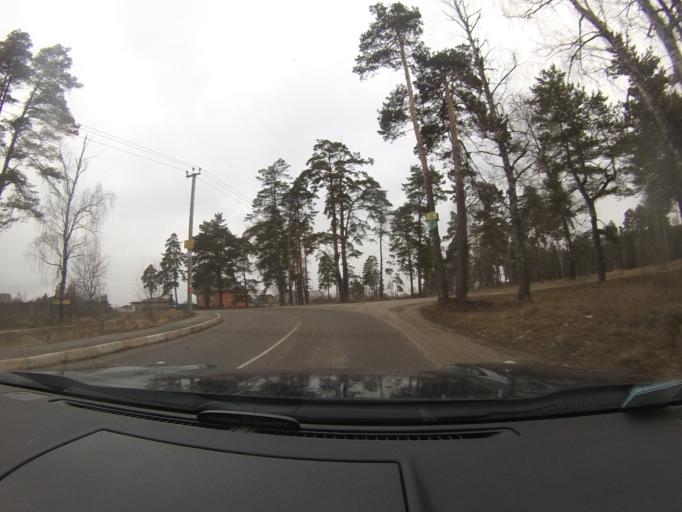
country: RU
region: Moskovskaya
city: Peski
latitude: 55.2653
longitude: 38.7584
